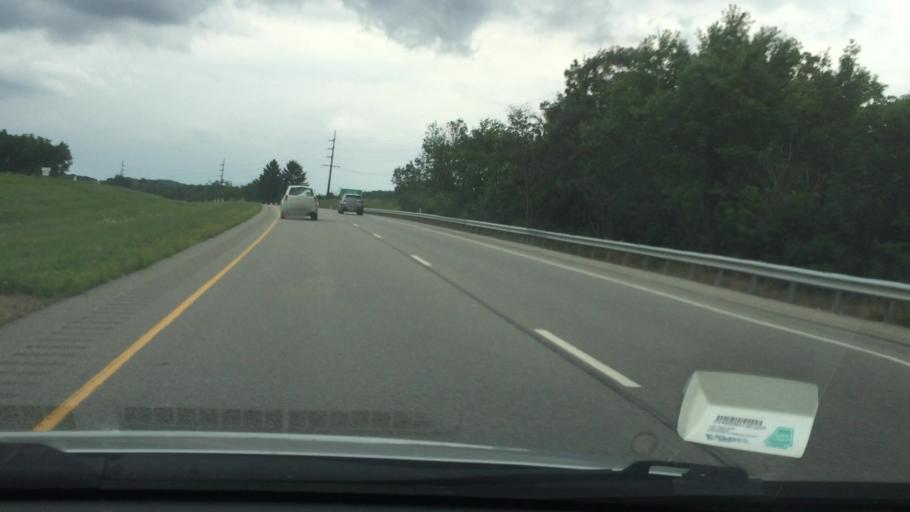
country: US
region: Pennsylvania
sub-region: Armstrong County
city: Freeport
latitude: 40.6827
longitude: -79.7141
